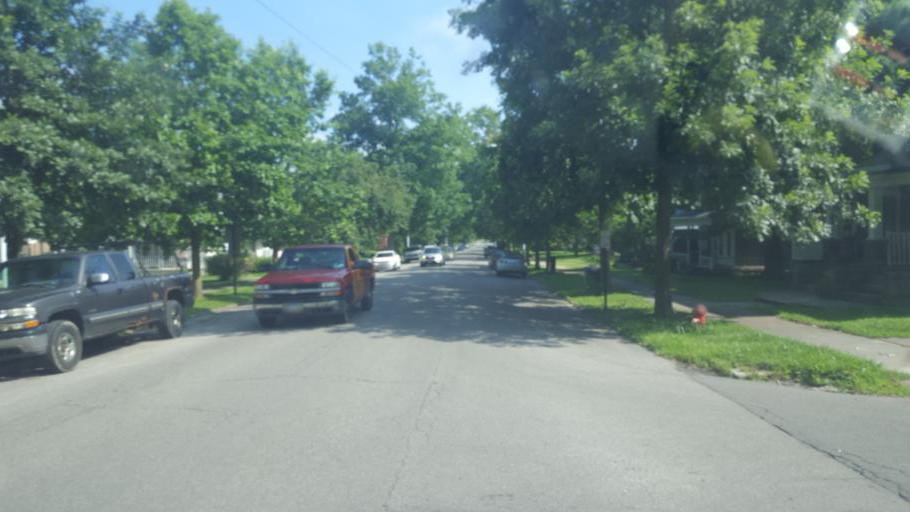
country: US
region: Ohio
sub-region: Crawford County
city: Galion
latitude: 40.7364
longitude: -82.7894
